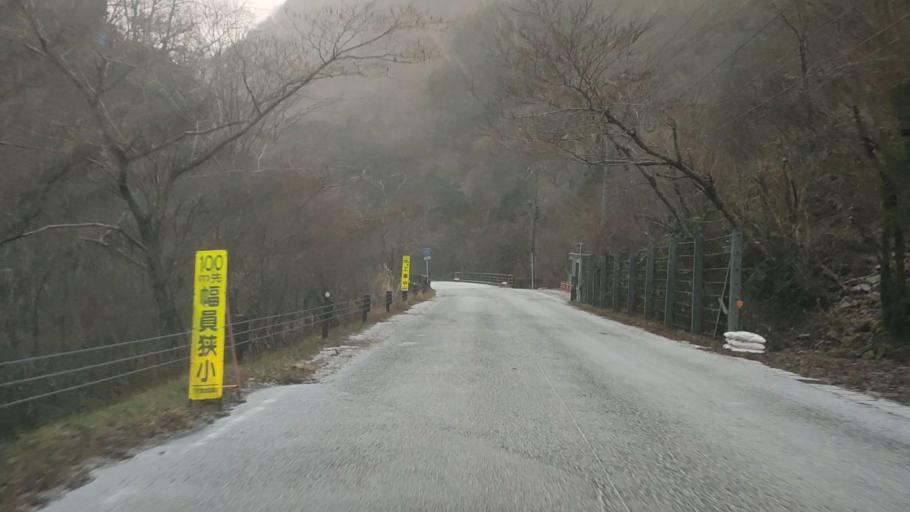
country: JP
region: Kumamoto
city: Matsubase
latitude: 32.5561
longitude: 130.9219
